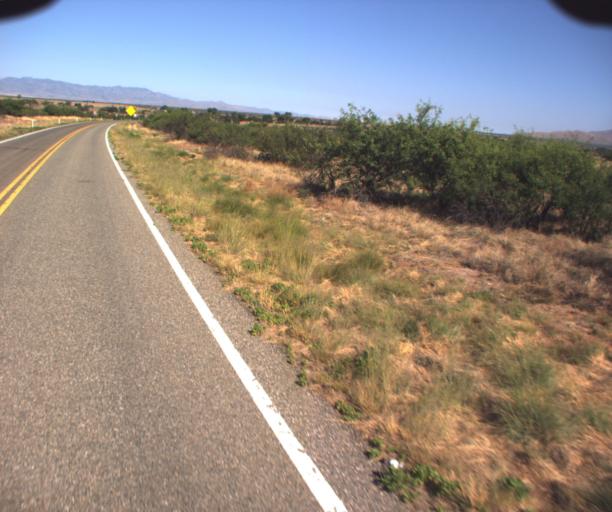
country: US
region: Arizona
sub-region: Graham County
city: Swift Trail Junction
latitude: 32.5823
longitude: -109.9531
